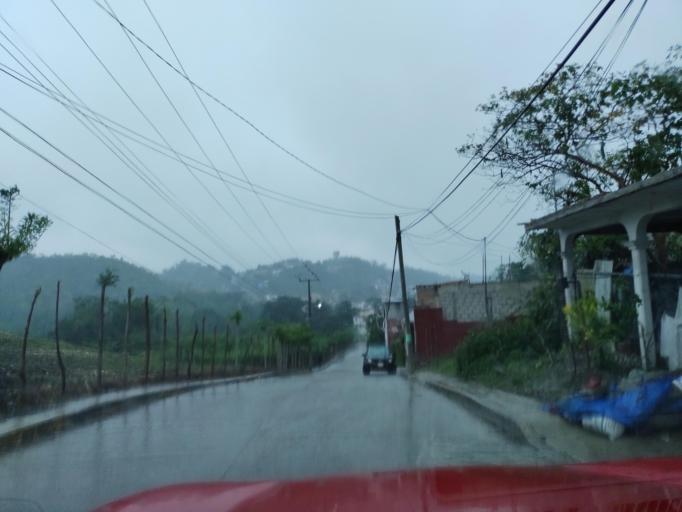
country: MX
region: Veracruz
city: Papantla de Olarte
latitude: 20.4389
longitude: -97.3367
